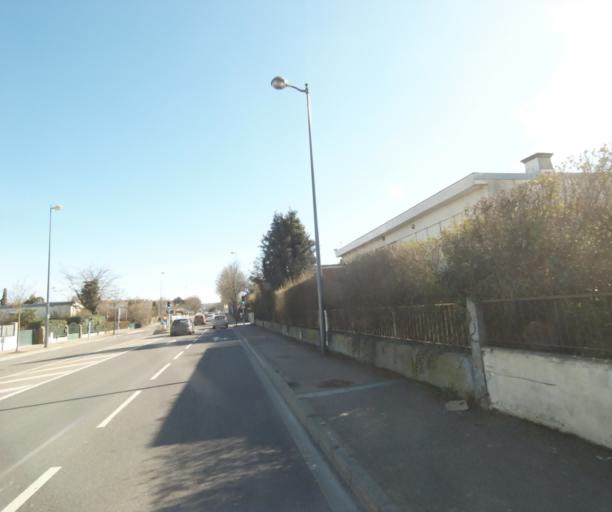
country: FR
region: Lorraine
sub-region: Departement de Meurthe-et-Moselle
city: Villers-les-Nancy
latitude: 48.6720
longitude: 6.1552
